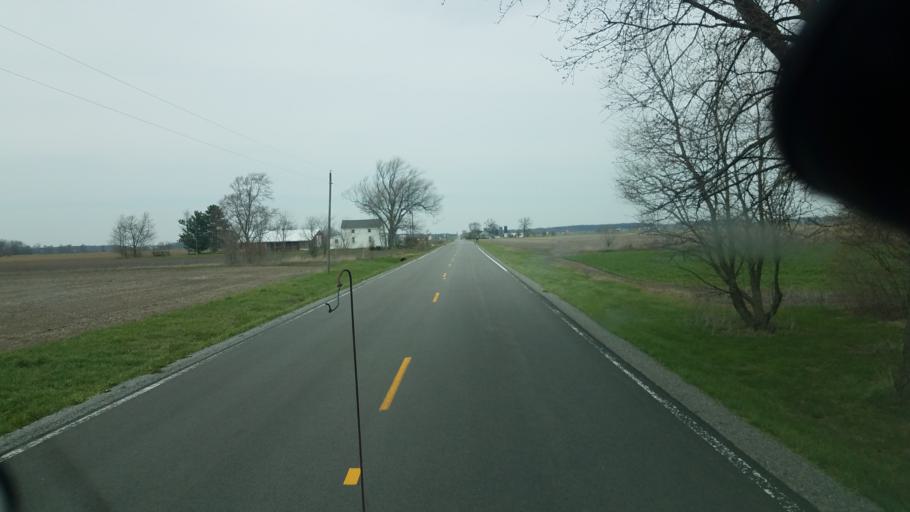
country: US
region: Ohio
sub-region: Wyandot County
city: Carey
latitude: 41.0128
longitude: -83.4776
